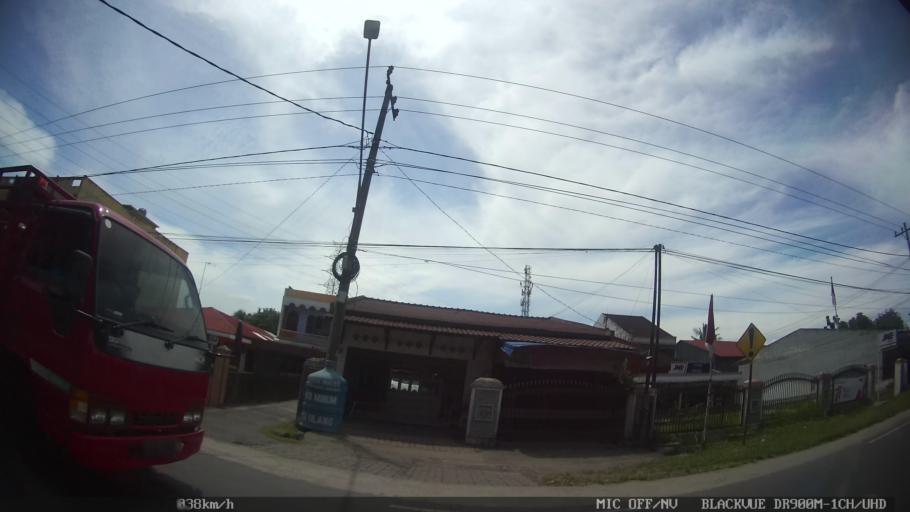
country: ID
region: North Sumatra
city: Binjai
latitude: 3.6225
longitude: 98.5037
